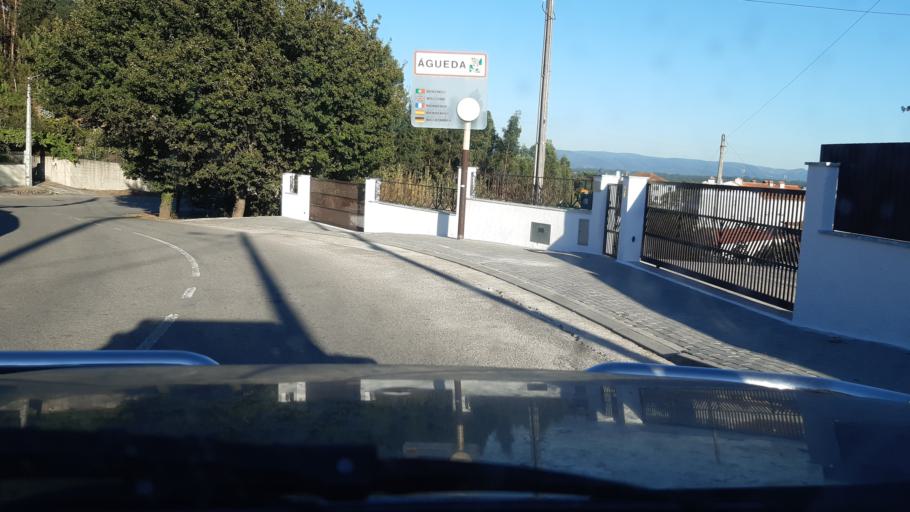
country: PT
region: Aveiro
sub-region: Agueda
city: Agueda
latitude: 40.5771
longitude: -8.4604
